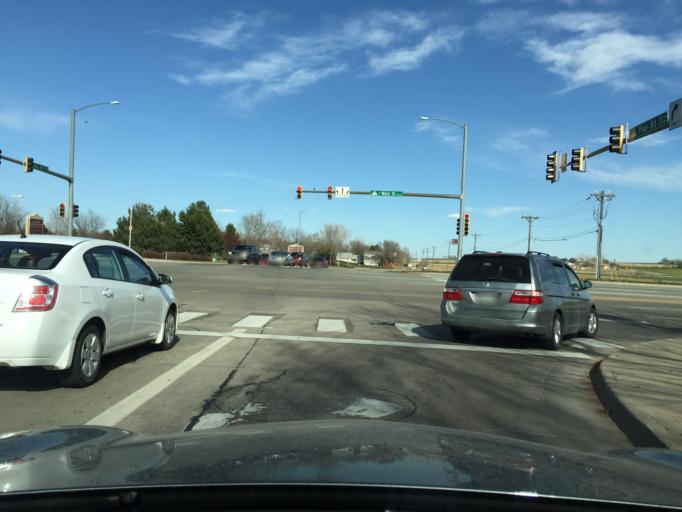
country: US
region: Colorado
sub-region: Boulder County
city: Longmont
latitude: 40.1382
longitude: -105.1028
